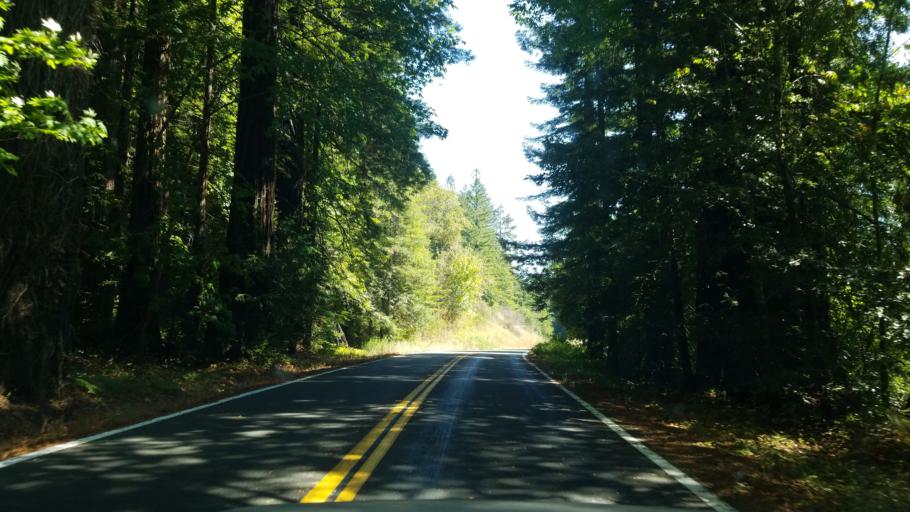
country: US
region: California
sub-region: Humboldt County
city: Redway
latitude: 40.3317
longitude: -123.9292
